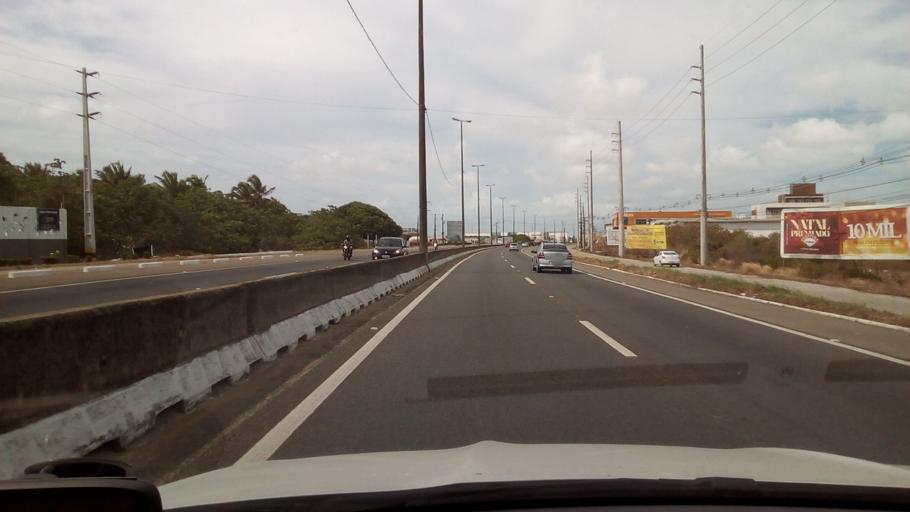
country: BR
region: Paraiba
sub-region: Joao Pessoa
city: Joao Pessoa
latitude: -7.0570
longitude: -34.8507
